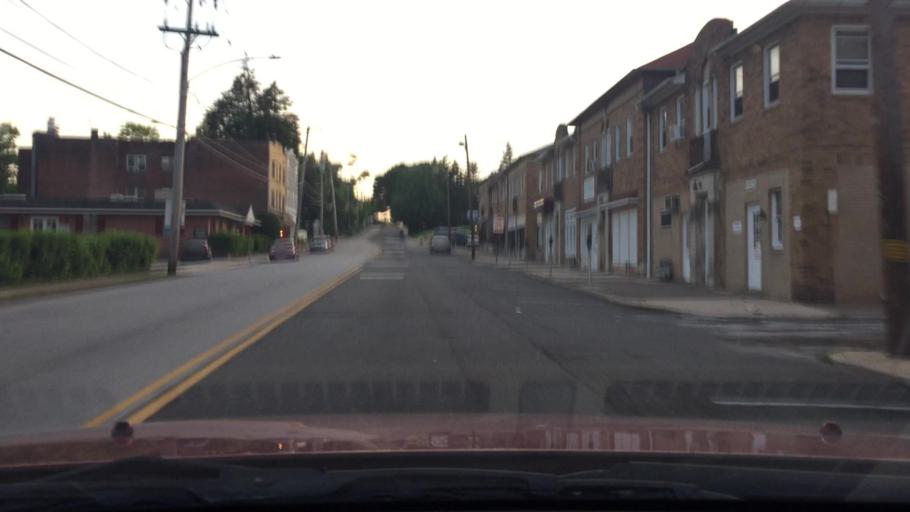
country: US
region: Pennsylvania
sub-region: Delaware County
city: Drexel Hill
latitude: 39.9511
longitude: -75.2830
